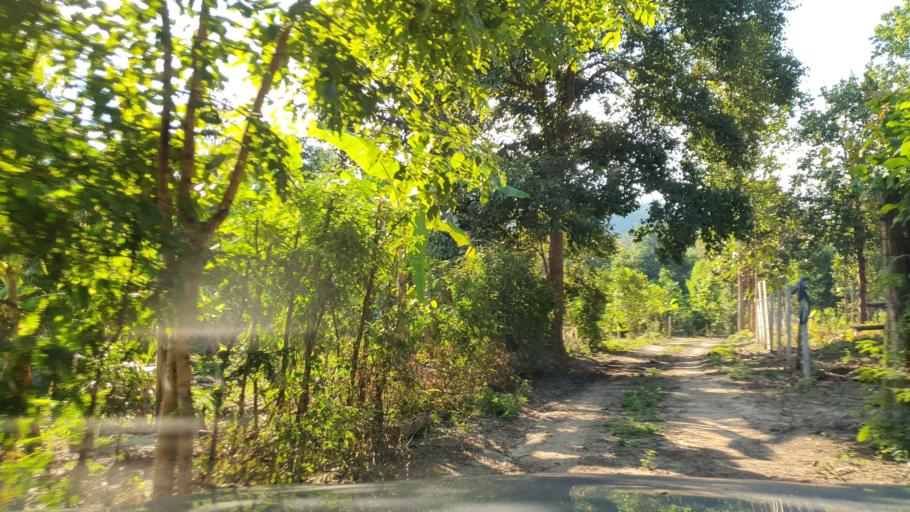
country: TH
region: Chiang Mai
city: Hang Dong
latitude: 18.7220
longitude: 98.8526
